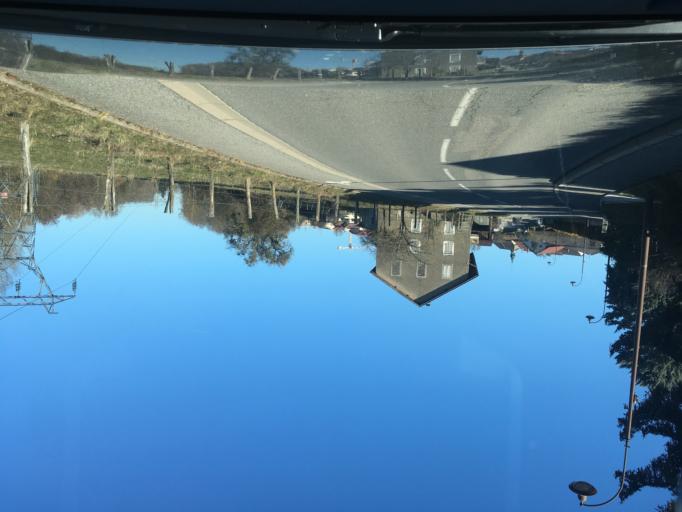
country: FR
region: Rhone-Alpes
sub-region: Departement de la Haute-Savoie
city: Cranves-Sales
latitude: 46.1837
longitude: 6.2949
